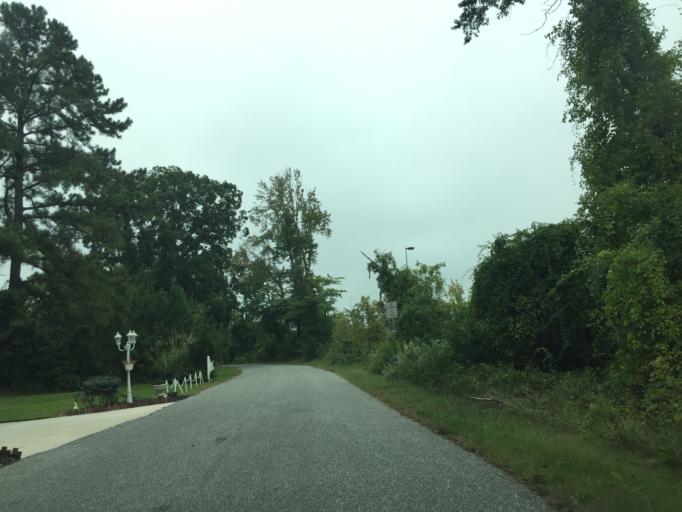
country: US
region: Maryland
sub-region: Baltimore County
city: Bowleys Quarters
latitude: 39.3463
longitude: -76.4020
